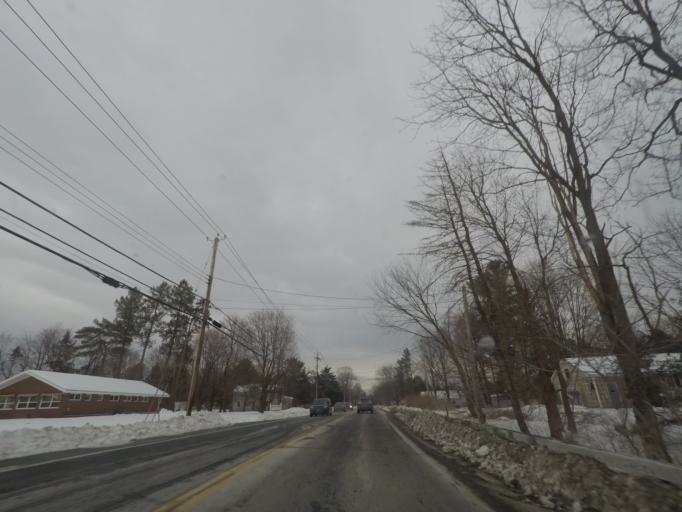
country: US
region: New York
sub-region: Columbia County
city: Kinderhook
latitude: 42.3860
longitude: -73.7167
